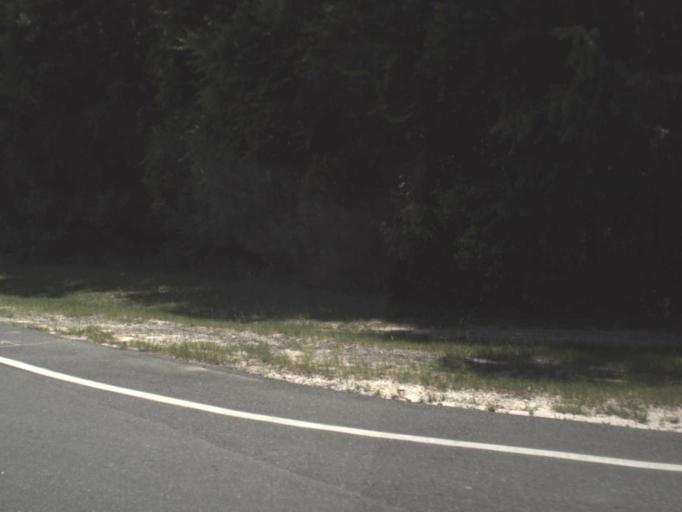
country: US
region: Florida
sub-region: Levy County
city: Manatee Road
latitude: 29.6369
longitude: -82.9835
